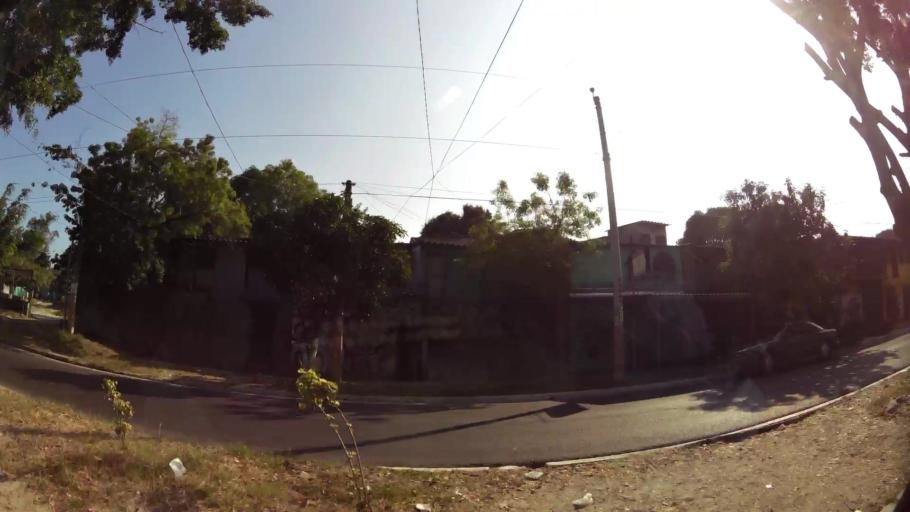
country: SV
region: San Salvador
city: Ilopango
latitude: 13.7162
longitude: -89.1066
